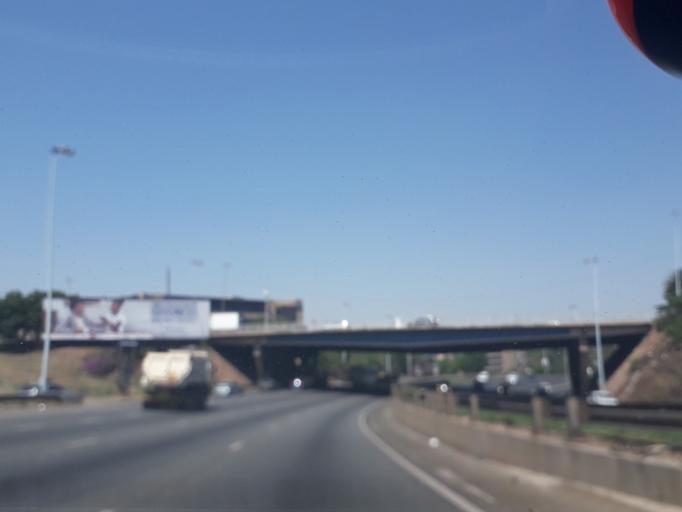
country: ZA
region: Gauteng
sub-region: City of Johannesburg Metropolitan Municipality
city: Johannesburg
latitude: -26.1831
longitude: 28.0329
